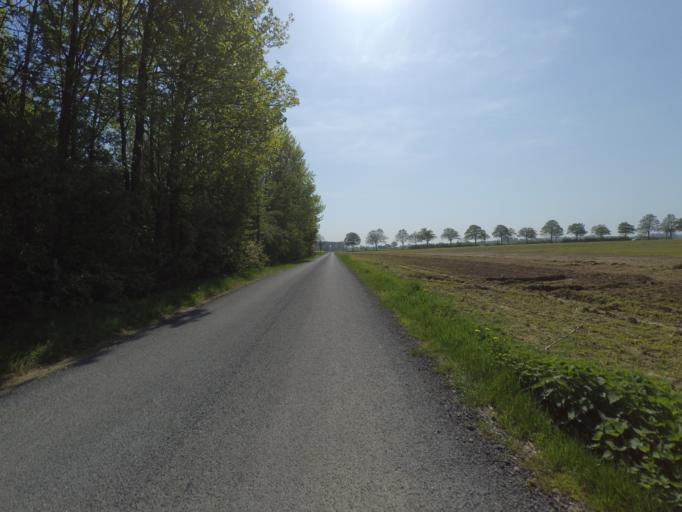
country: DE
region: North Rhine-Westphalia
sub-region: Regierungsbezirk Dusseldorf
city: Mehrhoog
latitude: 51.7139
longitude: 6.5007
